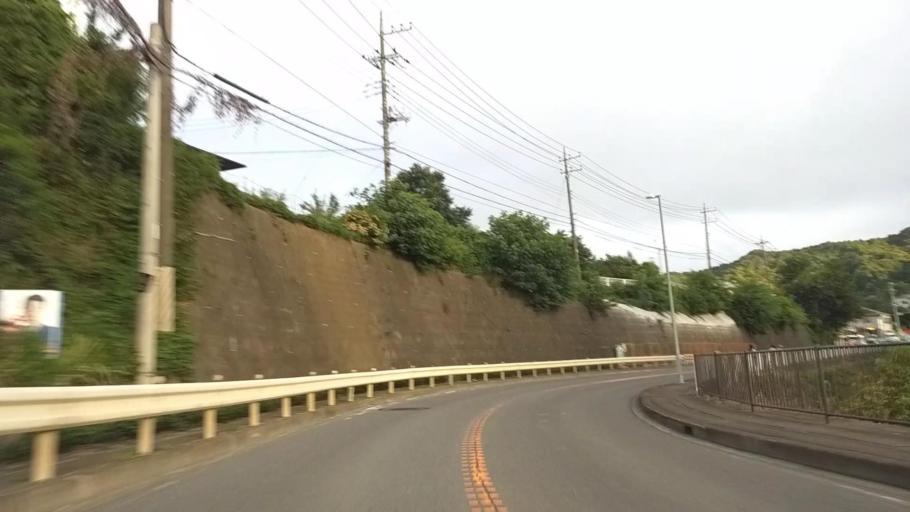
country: JP
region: Kanagawa
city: Atsugi
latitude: 35.4738
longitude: 139.3111
